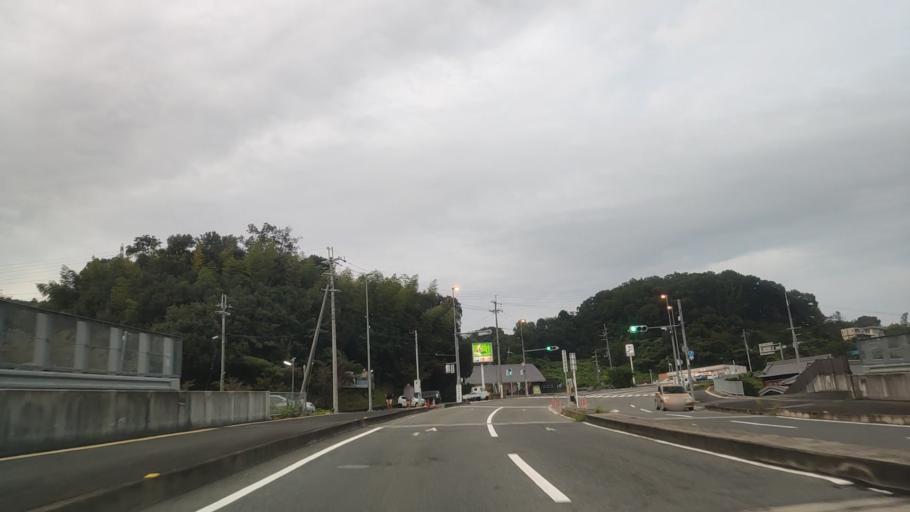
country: JP
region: Wakayama
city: Hashimoto
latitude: 34.3166
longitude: 135.6019
